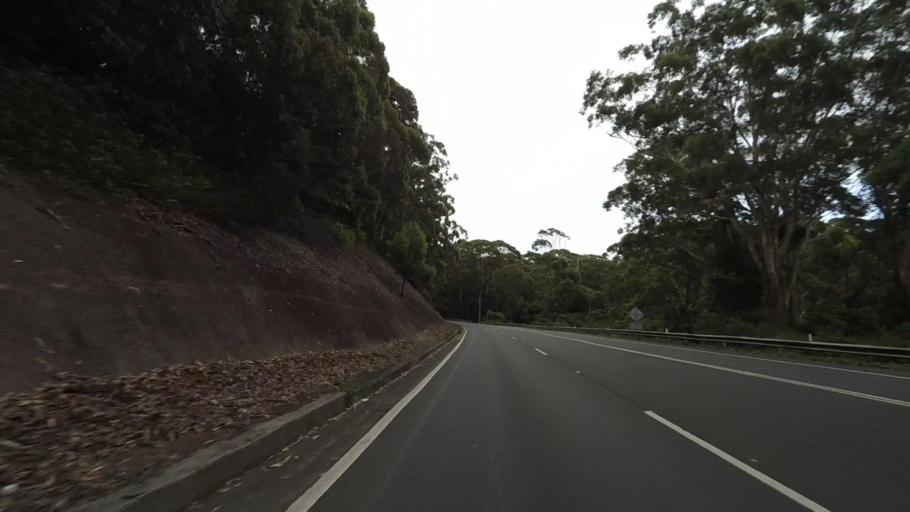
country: AU
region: New South Wales
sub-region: Wollongong
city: Bulli
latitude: -34.3168
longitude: 150.9028
